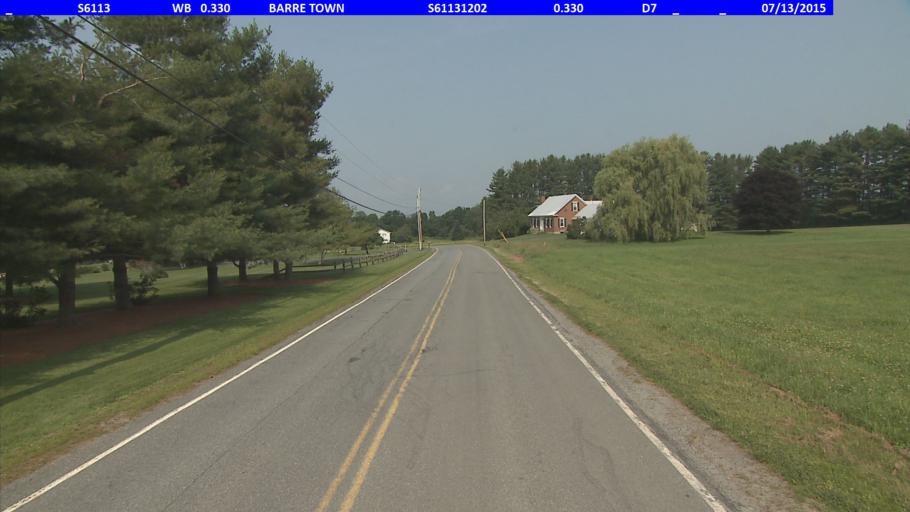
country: US
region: Vermont
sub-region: Washington County
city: Barre
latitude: 44.2203
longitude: -72.4660
